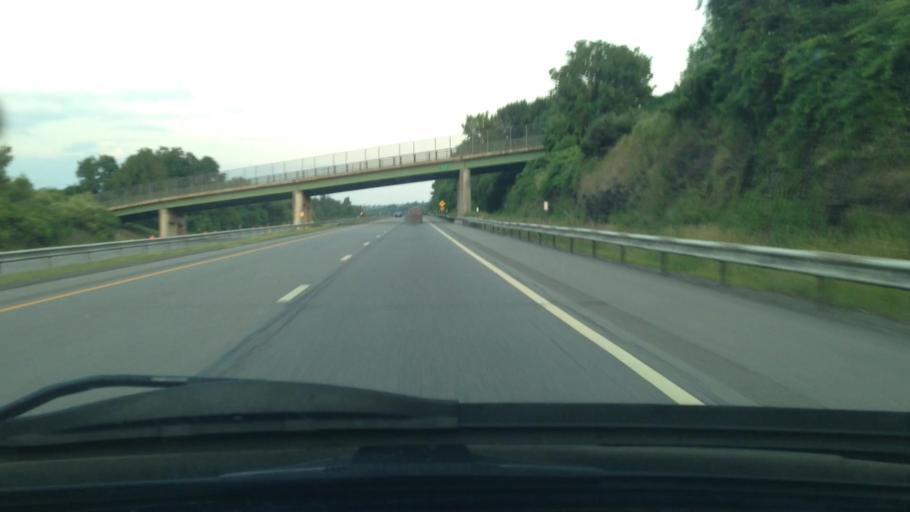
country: US
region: New York
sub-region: Montgomery County
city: Saint Johnsville
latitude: 42.9977
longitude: -74.7470
